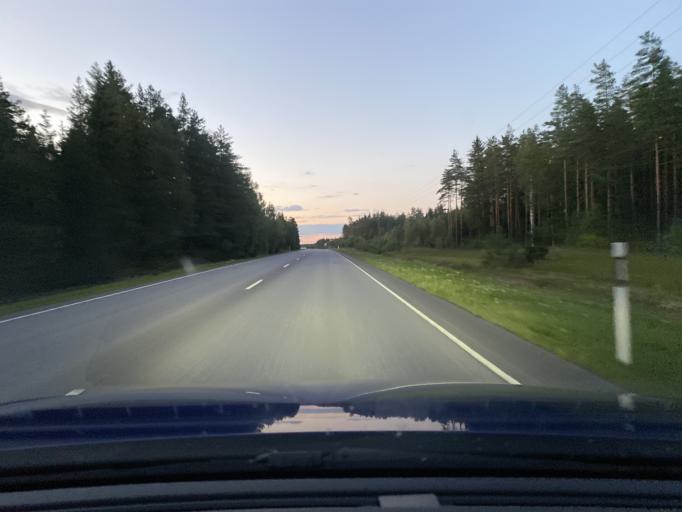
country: FI
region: Varsinais-Suomi
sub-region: Loimaa
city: Poeytyae
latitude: 60.7382
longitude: 22.5967
